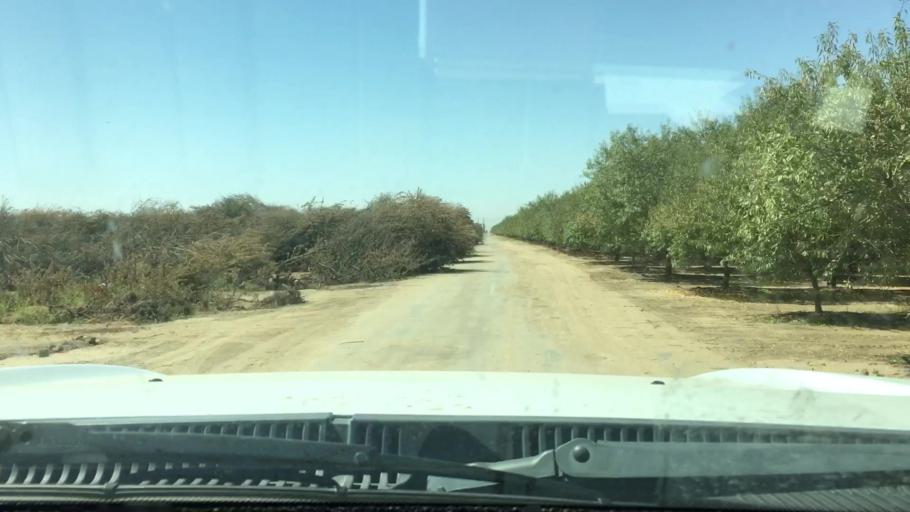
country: US
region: California
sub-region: Kern County
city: Shafter
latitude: 35.4563
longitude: -119.3067
